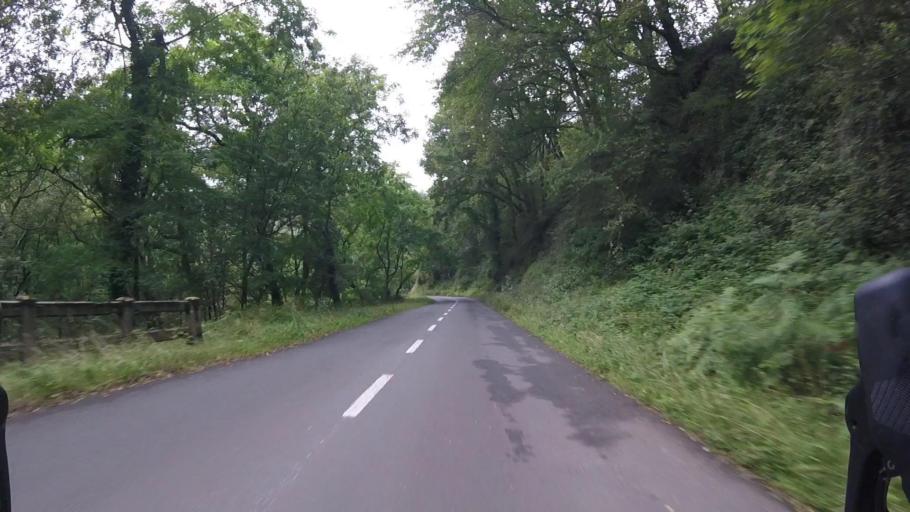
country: ES
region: Basque Country
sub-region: Provincia de Guipuzcoa
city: Irun
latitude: 43.2740
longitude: -1.8164
